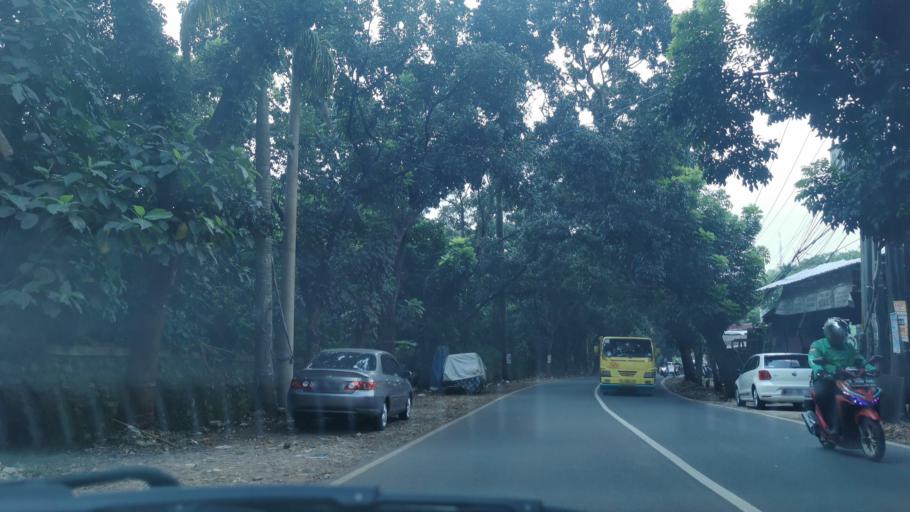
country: ID
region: West Java
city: Depok
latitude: -6.4093
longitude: 106.8318
